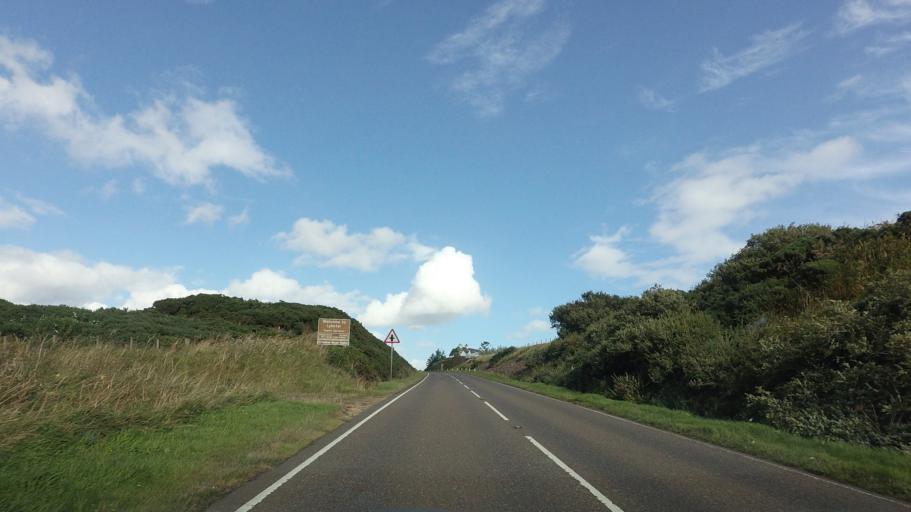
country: GB
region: Scotland
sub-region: Highland
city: Wick
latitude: 58.3047
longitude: -3.2955
